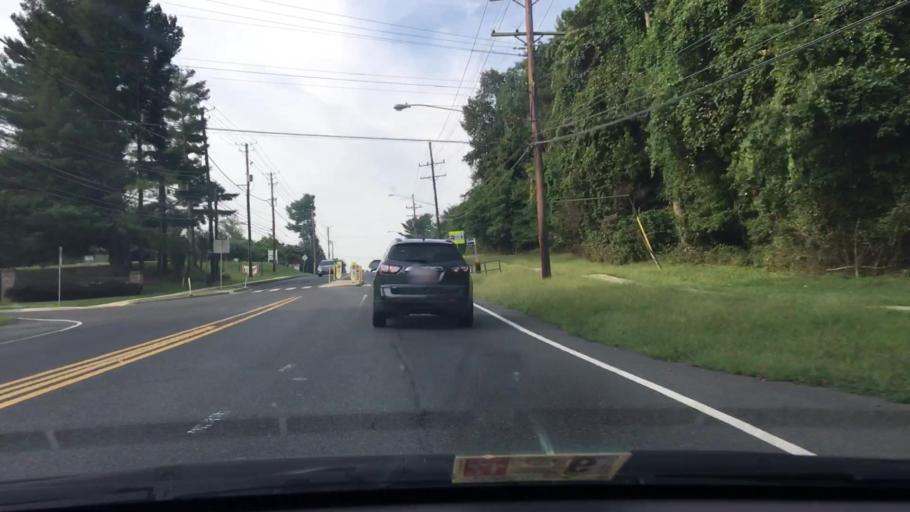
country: US
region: Maryland
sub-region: Montgomery County
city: Rockville
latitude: 39.0555
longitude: -77.1624
